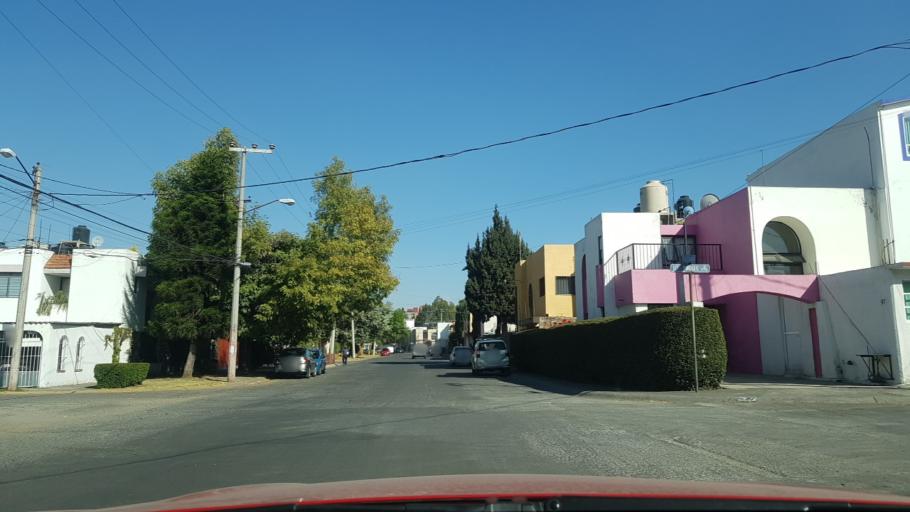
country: MX
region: Mexico
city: Cuautitlan Izcalli
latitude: 19.6462
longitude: -99.2030
